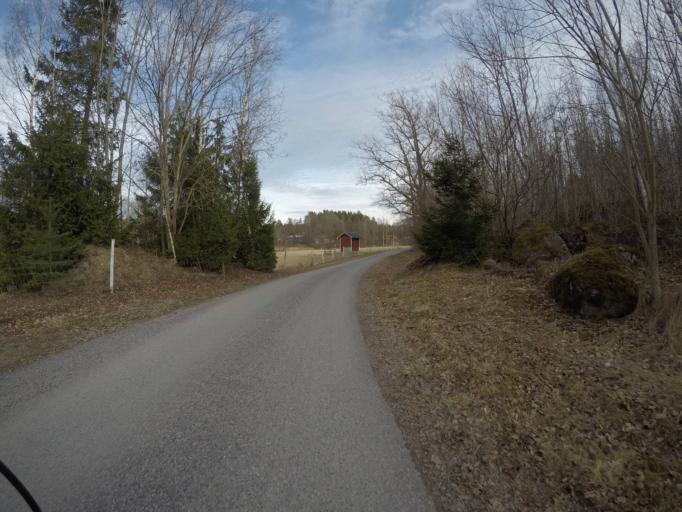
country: SE
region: Soedermanland
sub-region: Eskilstuna Kommun
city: Hallbybrunn
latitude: 59.4356
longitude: 16.4082
